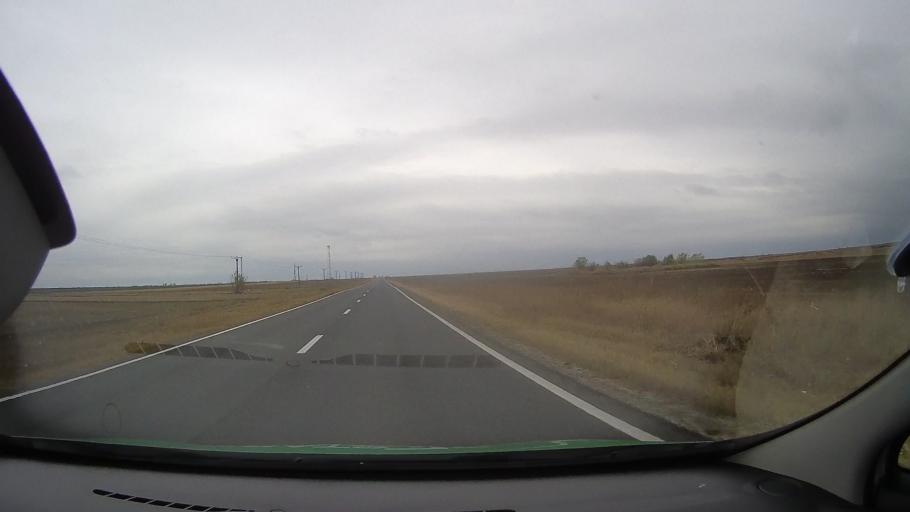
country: RO
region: Constanta
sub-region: Comuna Nicolae Balcescu
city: Nicolae Balcescu
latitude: 44.3762
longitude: 28.4207
